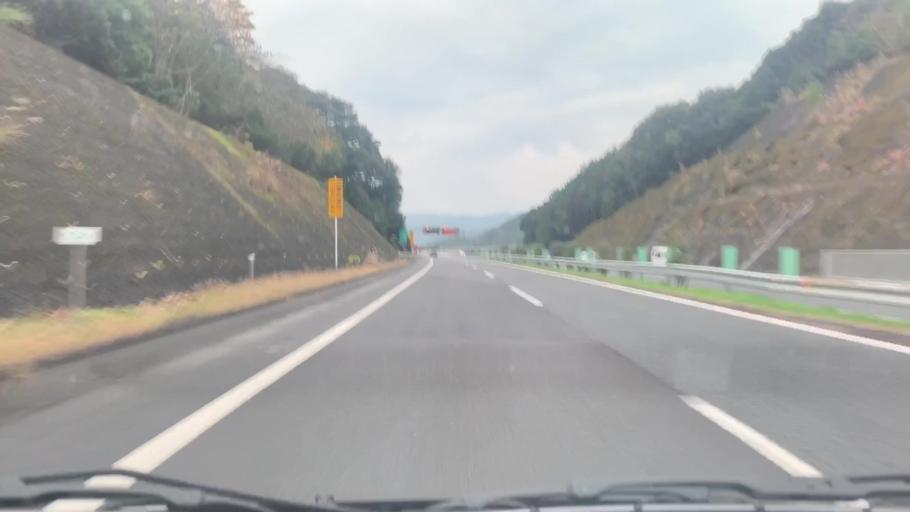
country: JP
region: Nagasaki
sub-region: Isahaya-shi
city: Isahaya
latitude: 32.8173
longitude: 129.9775
